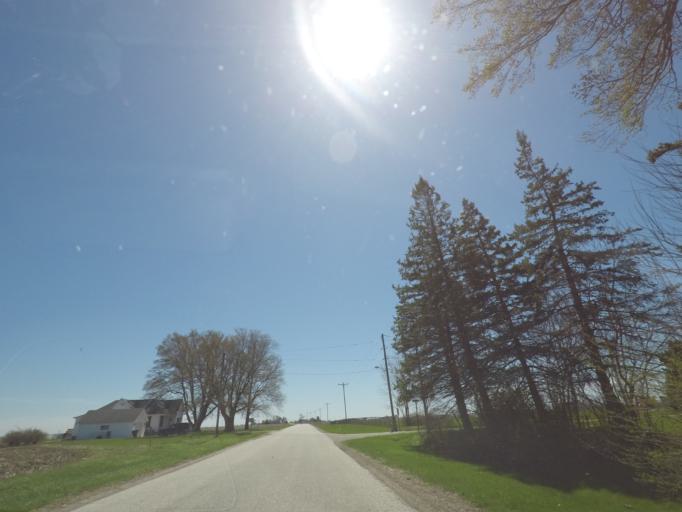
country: US
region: Illinois
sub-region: Logan County
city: Mount Pulaski
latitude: 40.0523
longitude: -89.1824
